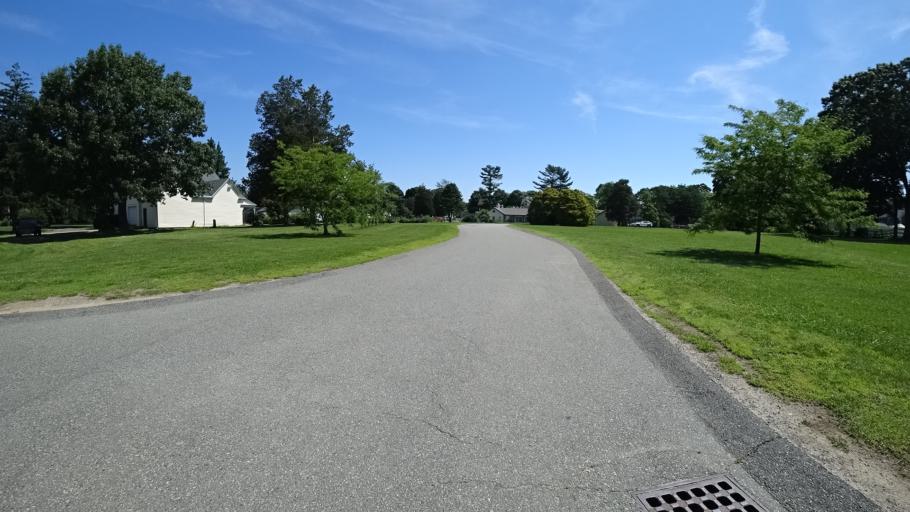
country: US
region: Massachusetts
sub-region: Norfolk County
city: Dedham
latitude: 42.2394
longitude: -71.1623
